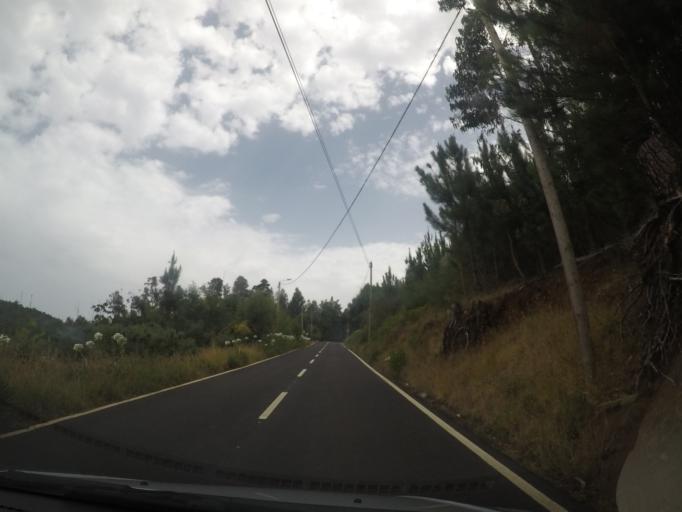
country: PT
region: Madeira
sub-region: Santa Cruz
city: Camacha
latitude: 32.6922
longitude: -16.8392
